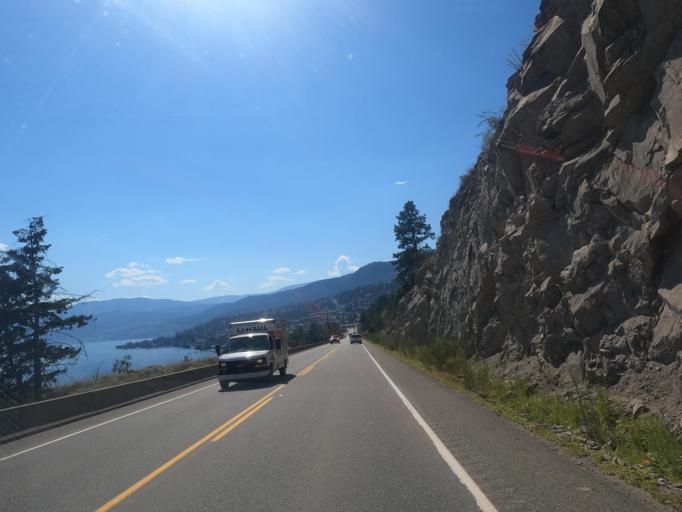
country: CA
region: British Columbia
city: Peachland
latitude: 49.7975
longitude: -119.6880
